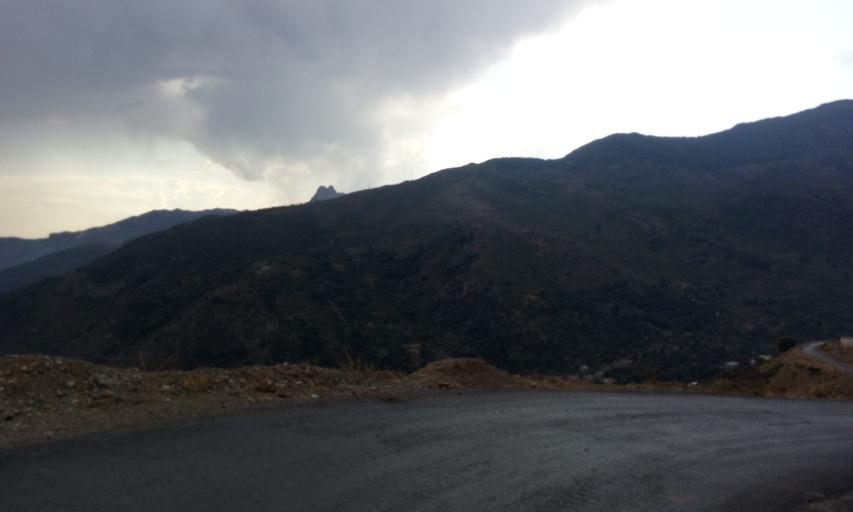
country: DZ
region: Tizi Ouzou
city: Chemini
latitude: 36.5975
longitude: 4.5804
